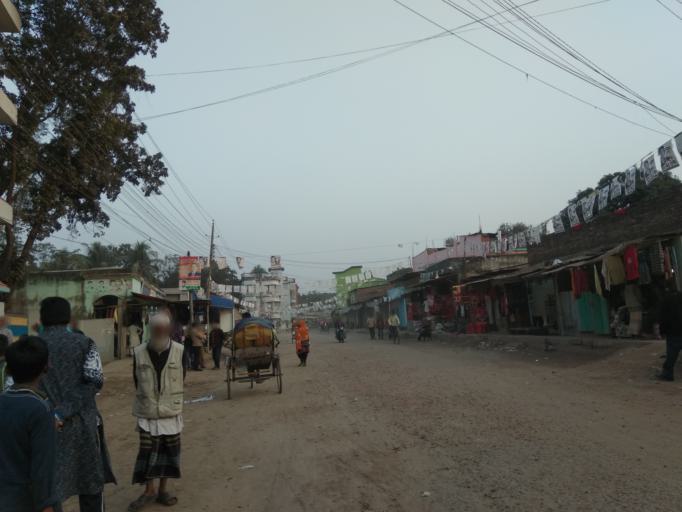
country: BD
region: Rangpur Division
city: Rangpur
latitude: 25.7309
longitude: 89.2650
